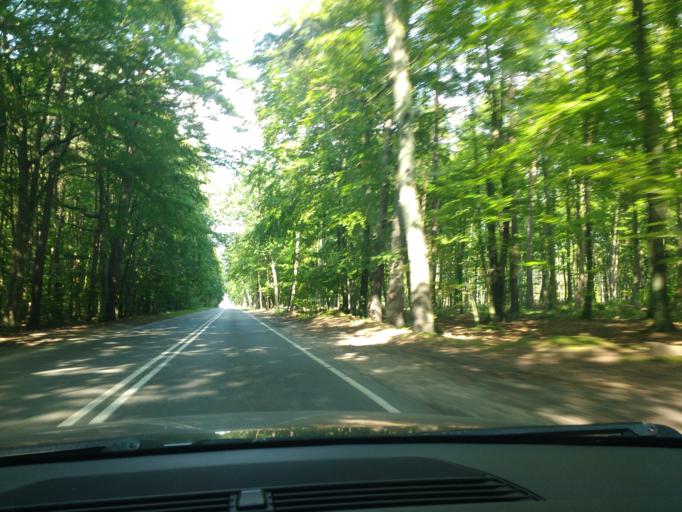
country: PL
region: Pomeranian Voivodeship
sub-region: Gdynia
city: Wielki Kack
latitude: 54.4613
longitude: 18.5086
